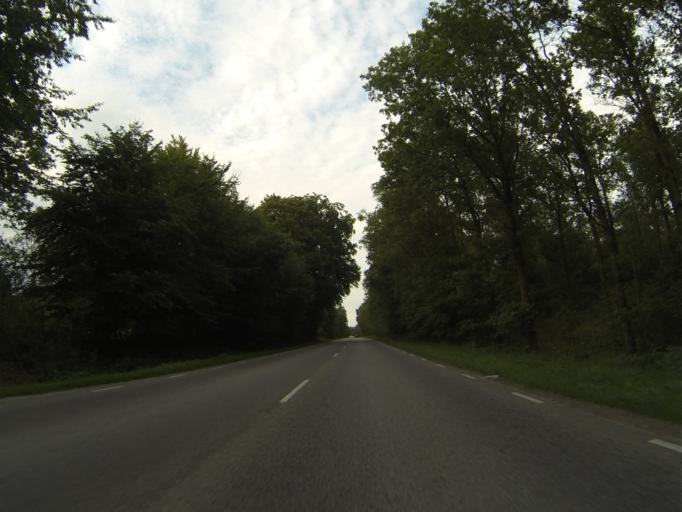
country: SE
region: Skane
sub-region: Lunds Kommun
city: Genarp
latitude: 55.6833
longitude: 13.3515
